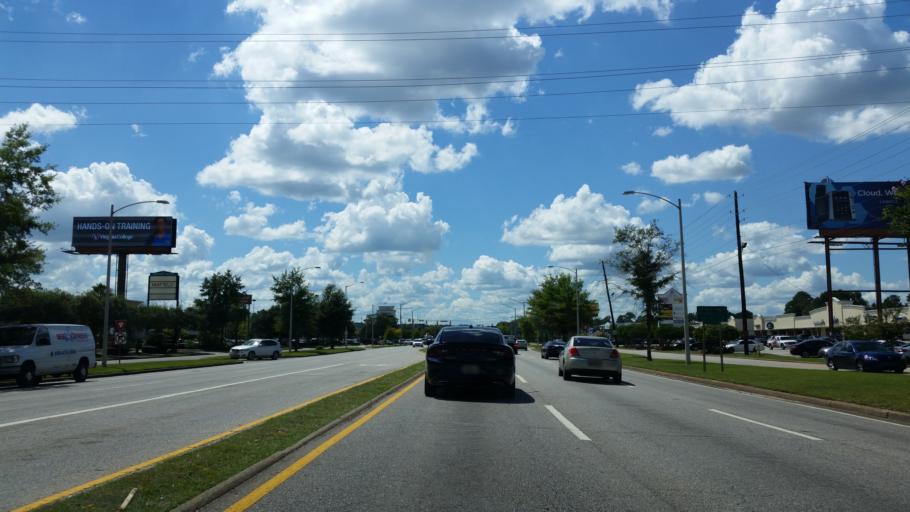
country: US
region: Alabama
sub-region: Mobile County
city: Prichard
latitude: 30.6761
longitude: -88.1325
